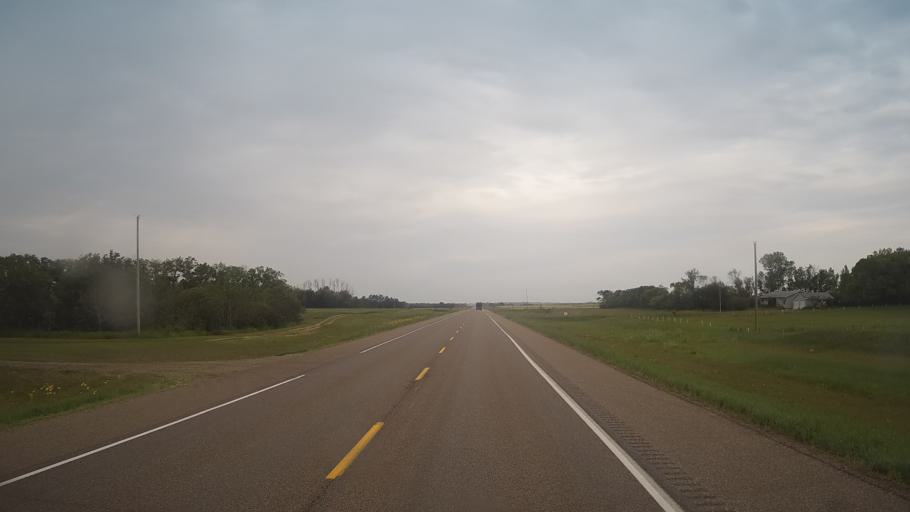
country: CA
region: Saskatchewan
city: Langham
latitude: 52.1294
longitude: -107.0681
